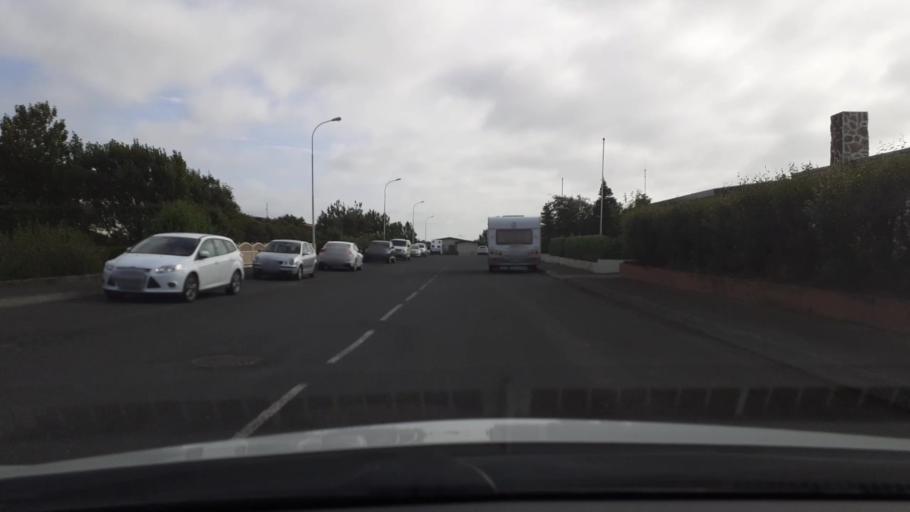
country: IS
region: South
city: THorlakshoefn
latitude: 63.8526
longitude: -21.3902
